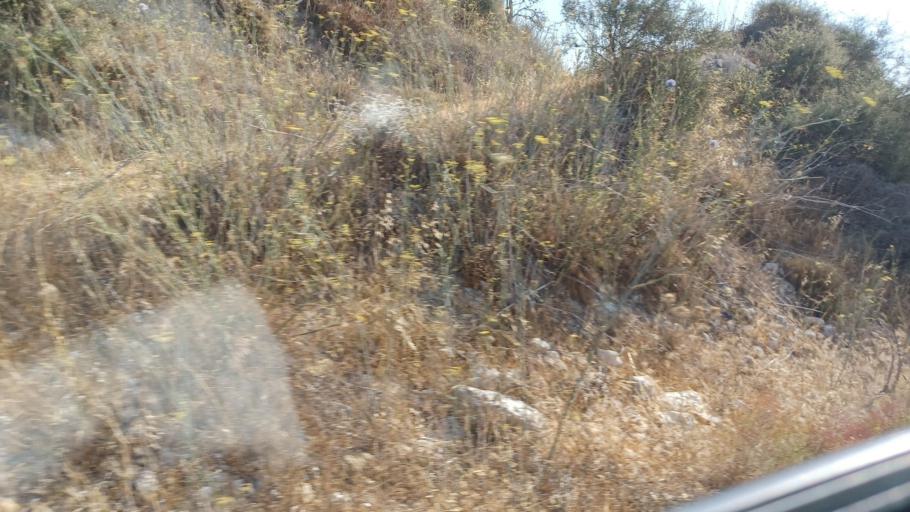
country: CY
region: Pafos
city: Tala
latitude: 34.8962
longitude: 32.4530
